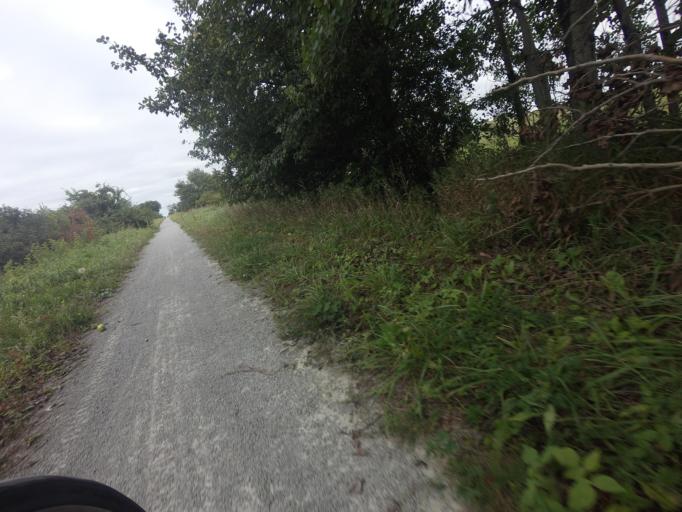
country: CA
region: Ontario
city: Omemee
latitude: 44.3249
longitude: -78.8061
